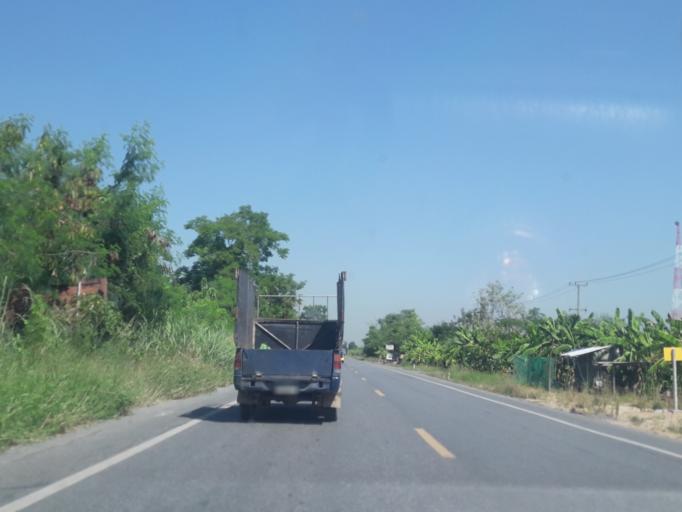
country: TH
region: Sara Buri
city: Nong Khae
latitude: 14.2524
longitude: 100.8234
